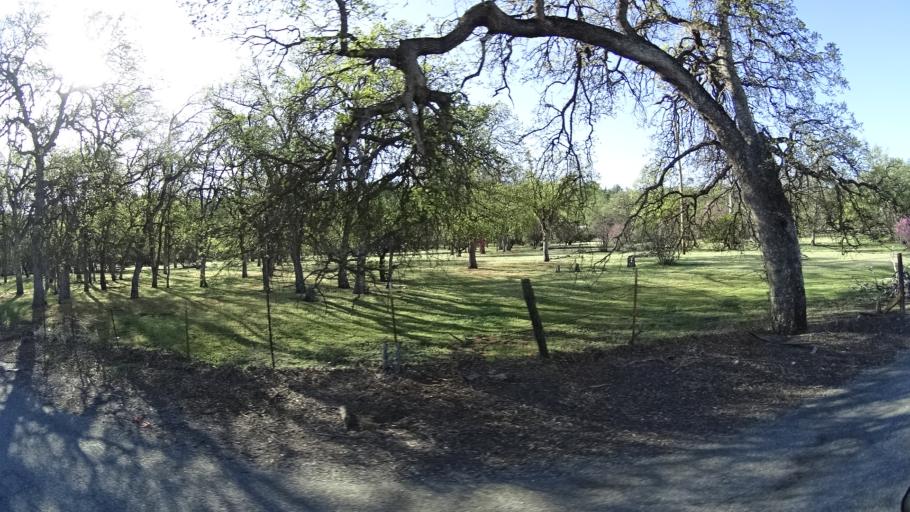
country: US
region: California
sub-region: Tehama County
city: Rancho Tehama Reserve
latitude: 39.7990
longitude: -122.4309
